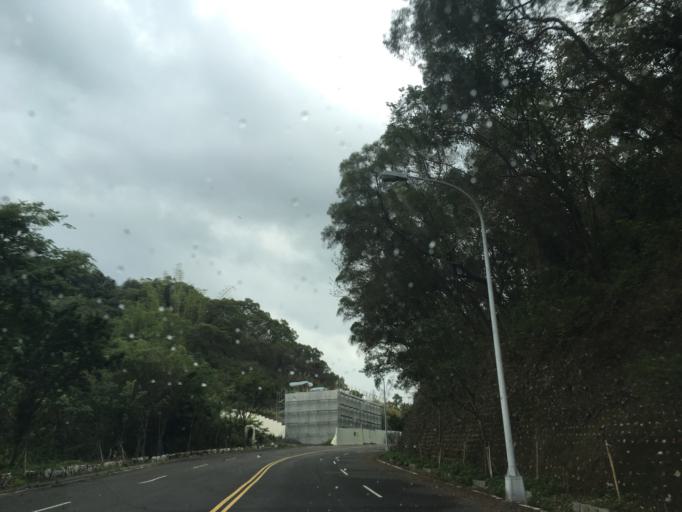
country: TW
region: Taiwan
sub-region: Taichung City
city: Taichung
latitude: 24.0631
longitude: 120.7246
